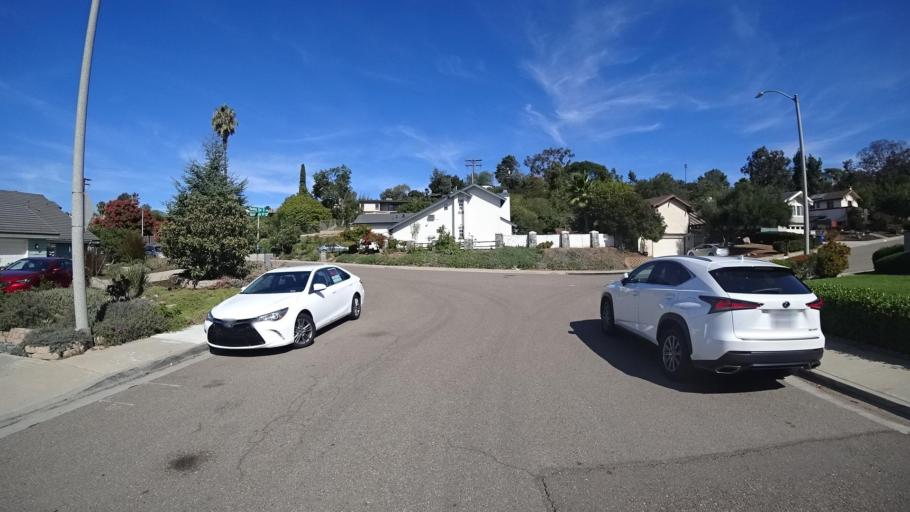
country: US
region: California
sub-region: San Diego County
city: Casa de Oro-Mount Helix
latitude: 32.7544
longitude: -116.9594
